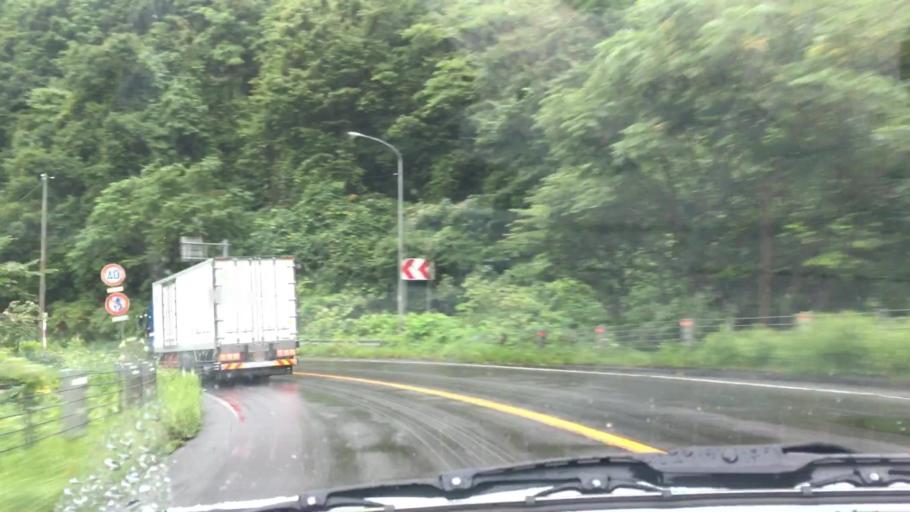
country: JP
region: Hokkaido
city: Niseko Town
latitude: 42.5946
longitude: 140.5933
